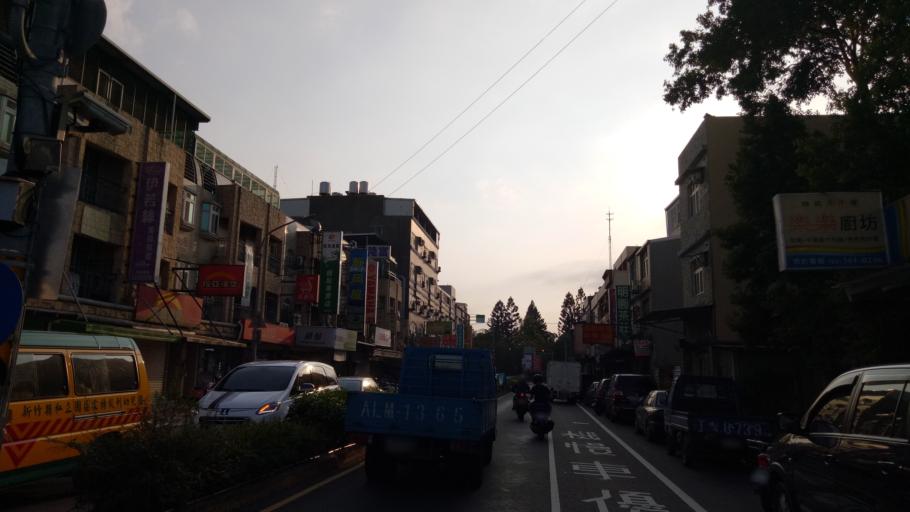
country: TW
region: Taiwan
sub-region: Hsinchu
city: Hsinchu
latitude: 24.7781
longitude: 120.9844
